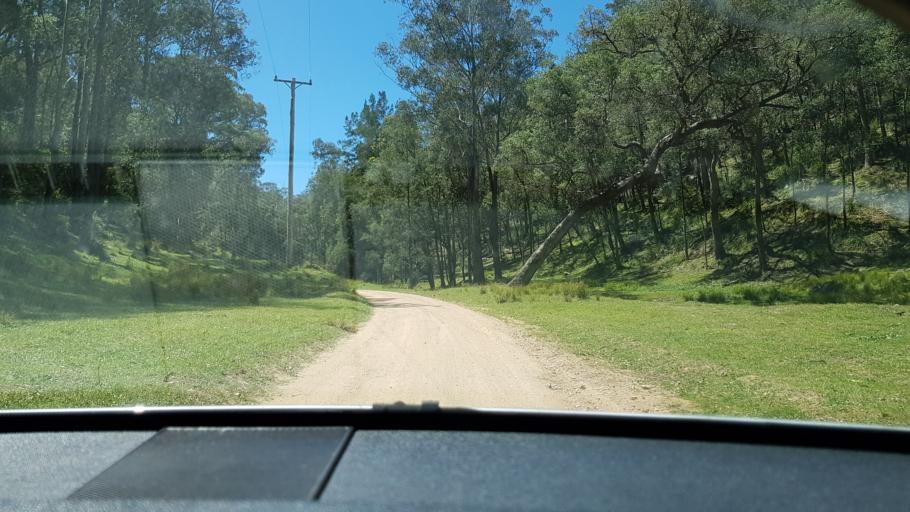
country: AU
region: New South Wales
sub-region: Blue Mountains Municipality
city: Katoomba
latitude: -33.7796
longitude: 150.2327
